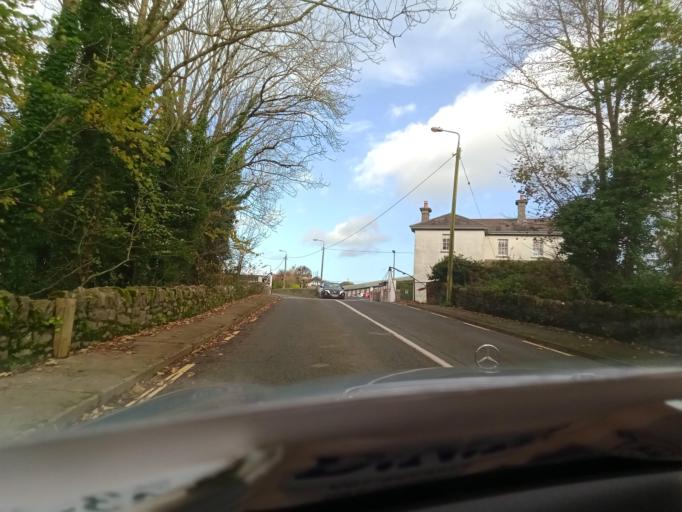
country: IE
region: Leinster
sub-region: Kilkenny
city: Piltown
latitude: 52.3298
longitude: -7.3144
